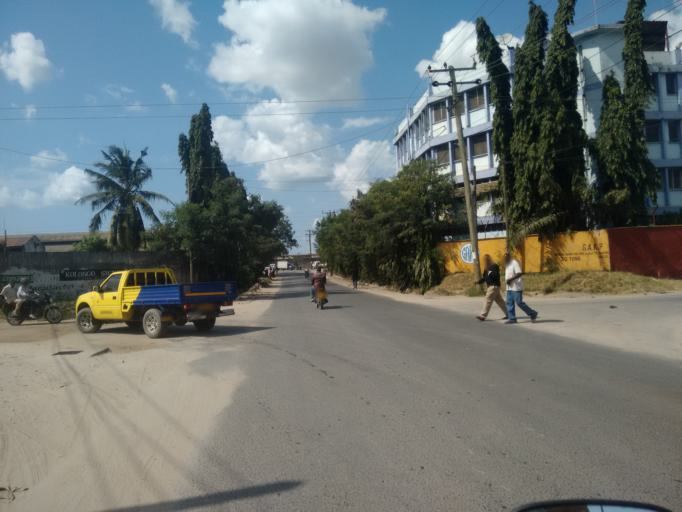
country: TZ
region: Dar es Salaam
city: Dar es Salaam
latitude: -6.8374
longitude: 39.2703
